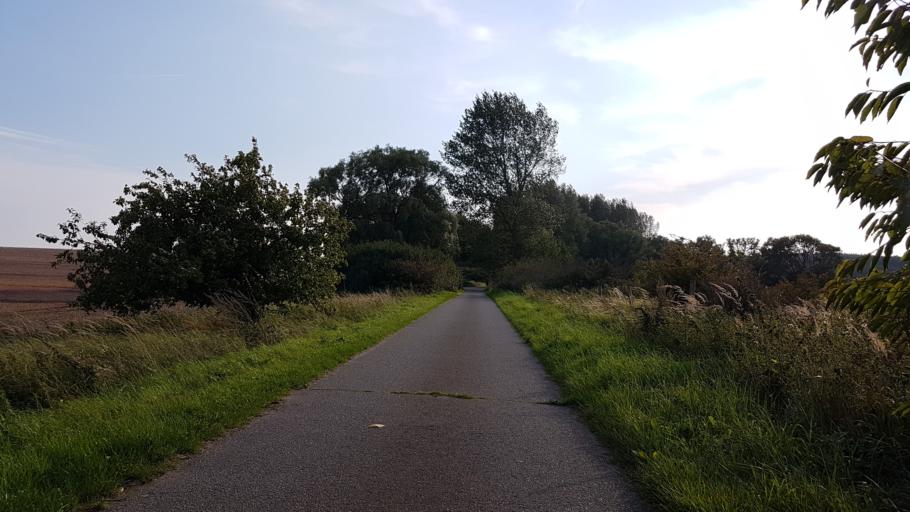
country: DE
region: Mecklenburg-Vorpommern
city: Sagard
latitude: 54.5121
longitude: 13.5282
